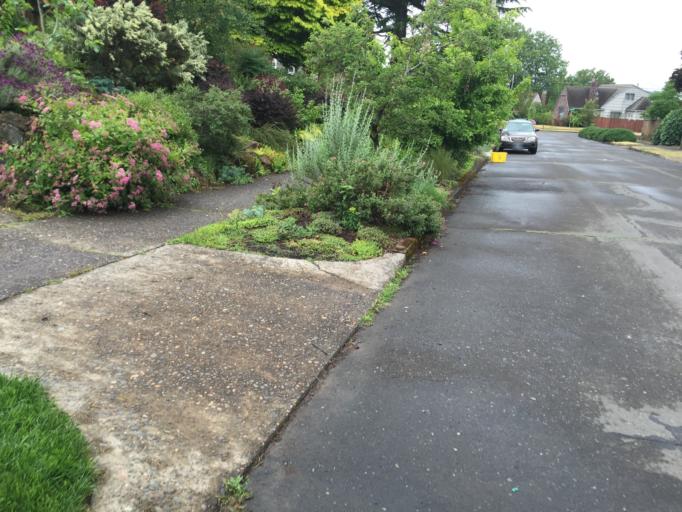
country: US
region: Oregon
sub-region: Multnomah County
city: Portland
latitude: 45.5322
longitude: -122.6116
